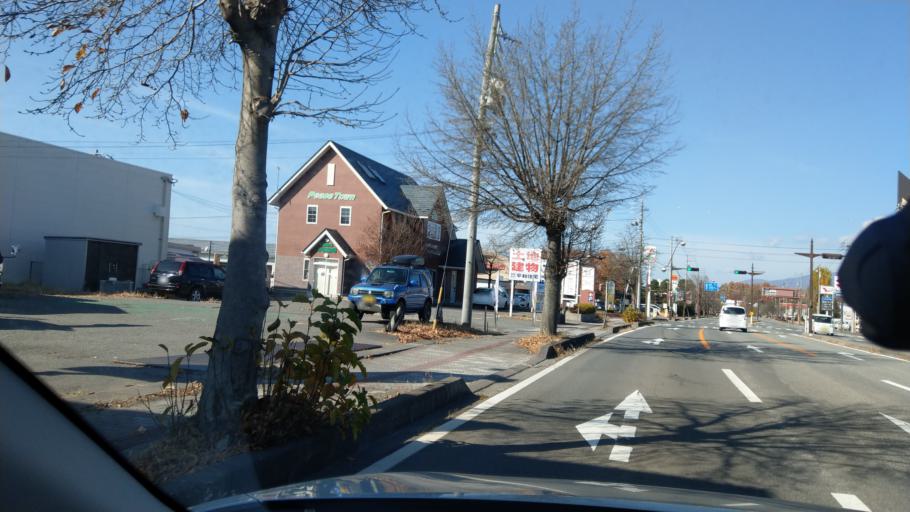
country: JP
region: Nagano
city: Komoro
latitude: 36.2845
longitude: 138.4810
